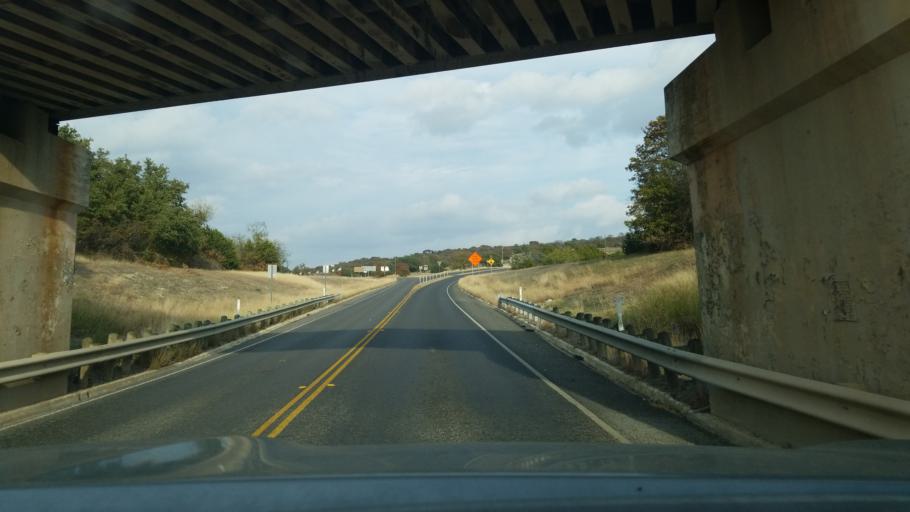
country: US
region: Texas
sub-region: Mills County
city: Goldthwaite
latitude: 31.4663
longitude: -98.5715
